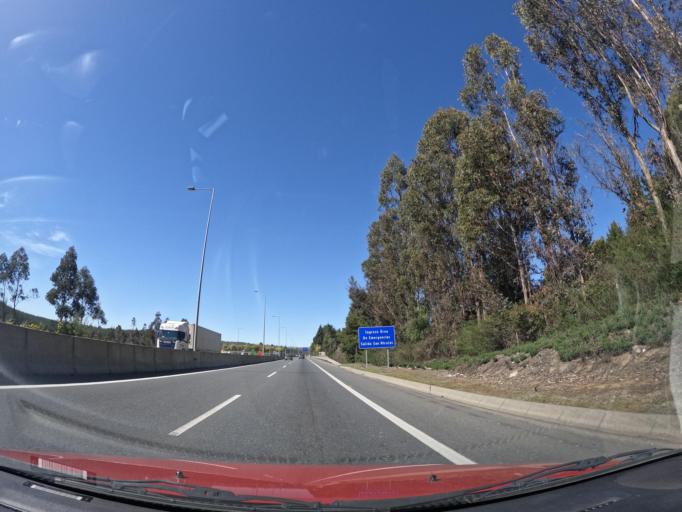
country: CL
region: Biobio
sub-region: Provincia de Concepcion
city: Chiguayante
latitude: -36.9049
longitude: -72.7877
